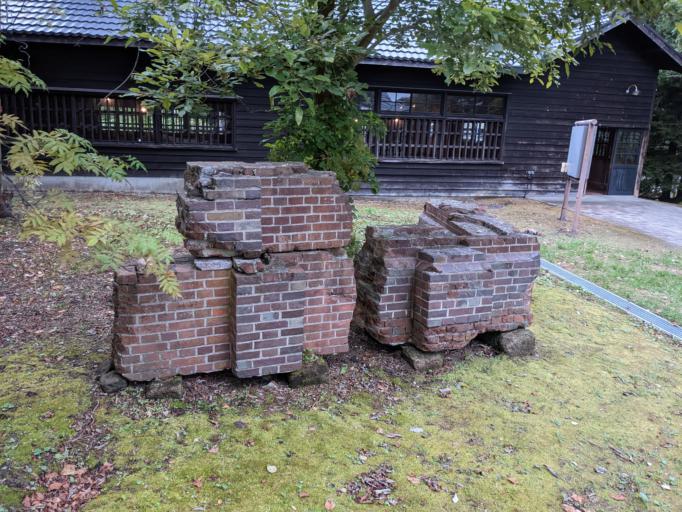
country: JP
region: Hokkaido
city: Abashiri
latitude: 43.9952
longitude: 144.2294
